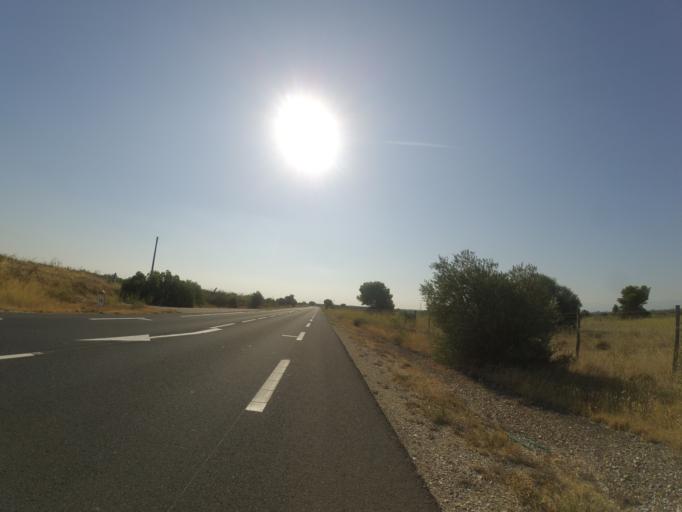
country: FR
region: Languedoc-Roussillon
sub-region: Departement des Pyrenees-Orientales
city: Rivesaltes
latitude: 42.7970
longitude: 2.8673
